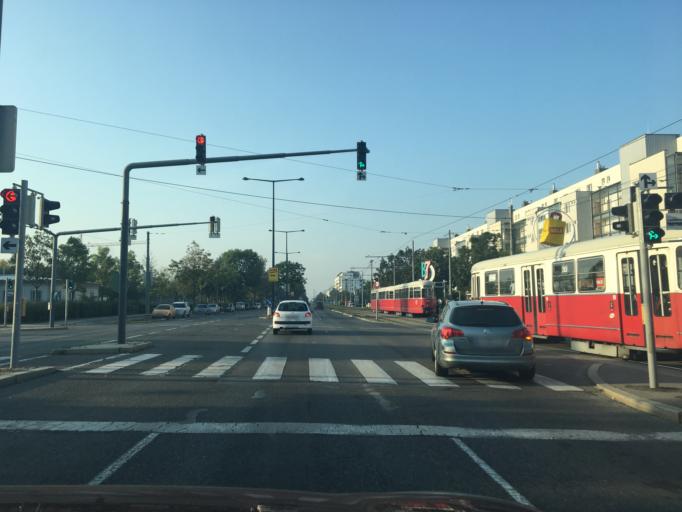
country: AT
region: Lower Austria
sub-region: Politischer Bezirk Korneuburg
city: Hagenbrunn
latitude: 48.2935
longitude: 16.4184
